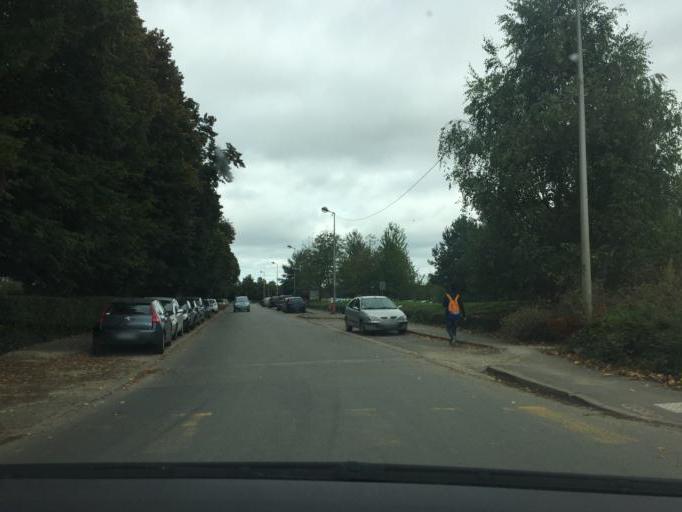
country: FR
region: Ile-de-France
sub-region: Departement de l'Essonne
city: Bures-sur-Yvette
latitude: 48.7099
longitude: 2.1721
